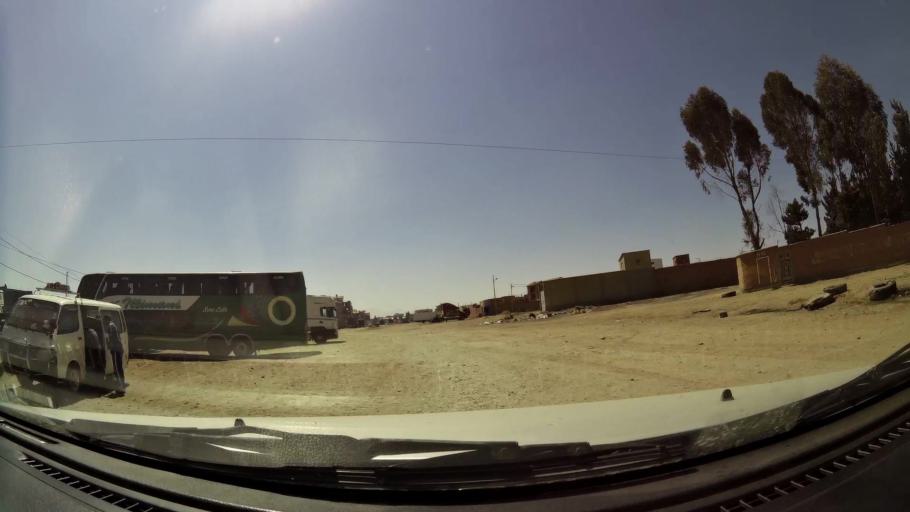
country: BO
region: La Paz
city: La Paz
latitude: -16.5503
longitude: -68.1835
